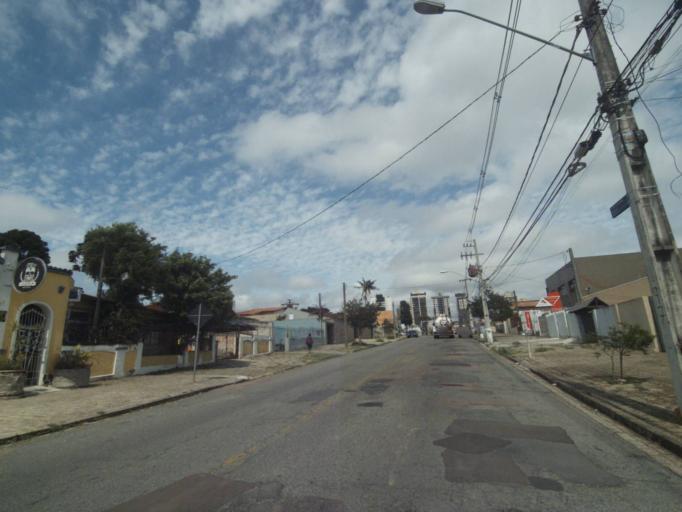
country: BR
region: Parana
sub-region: Pinhais
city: Pinhais
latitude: -25.4386
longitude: -49.2313
